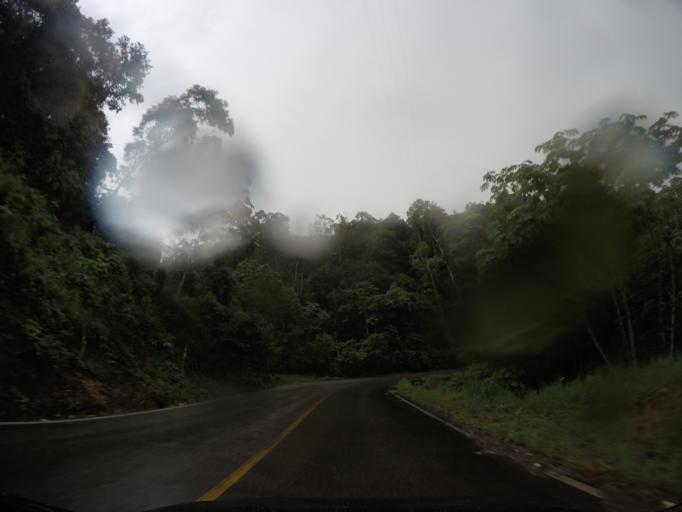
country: MX
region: Oaxaca
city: San Gabriel Mixtepec
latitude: 16.0813
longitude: -97.0790
